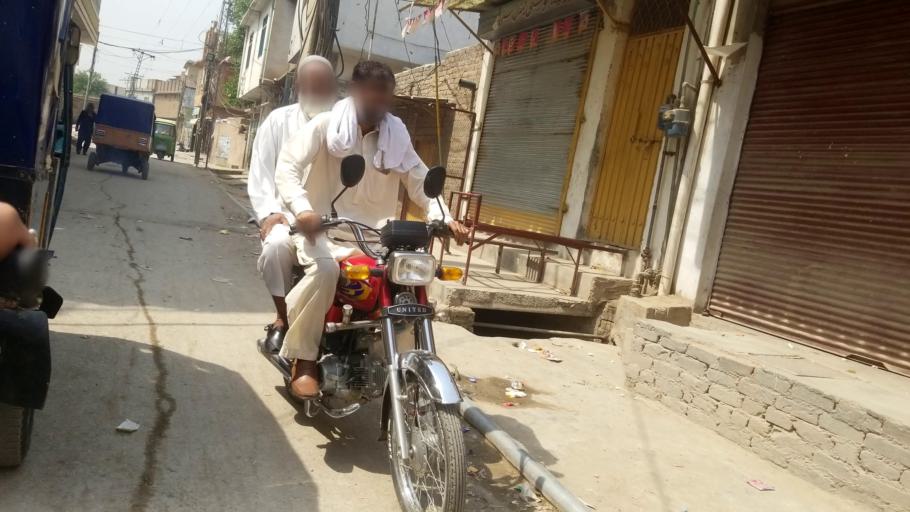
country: PK
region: Khyber Pakhtunkhwa
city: Peshawar
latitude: 33.9875
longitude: 71.5413
